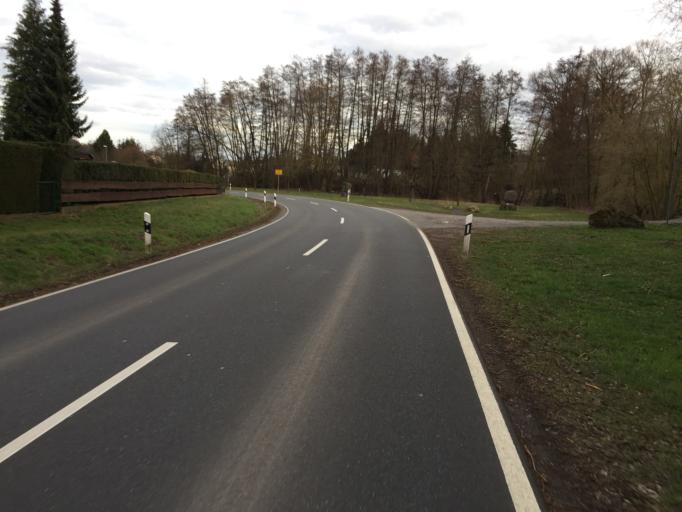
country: DE
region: Hesse
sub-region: Regierungsbezirk Giessen
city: Rabenau
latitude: 50.6763
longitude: 8.8535
